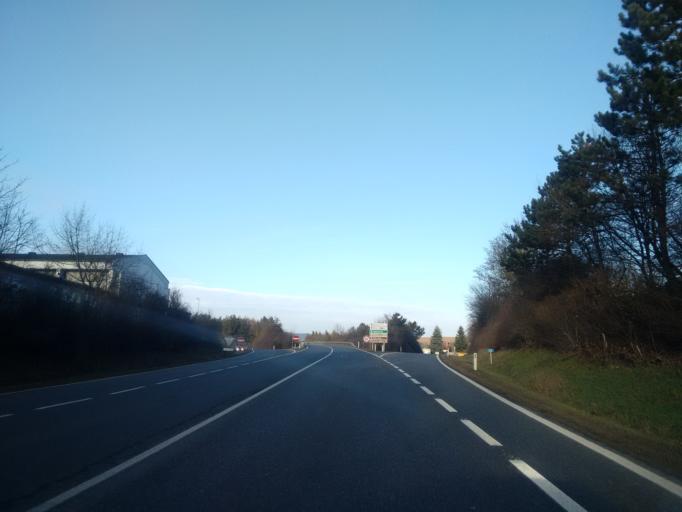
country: AT
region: Lower Austria
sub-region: Politischer Bezirk Melk
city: Melk
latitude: 48.2231
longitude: 15.3498
